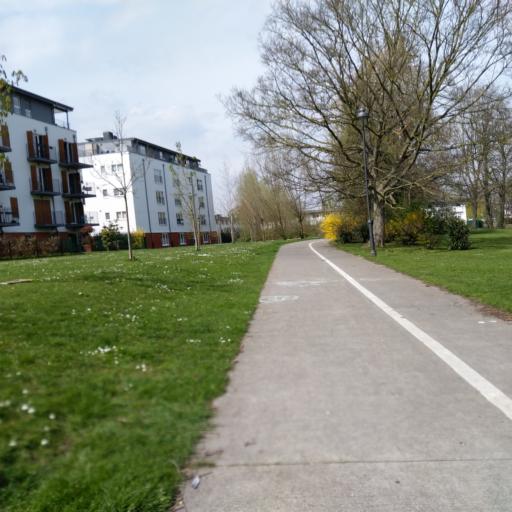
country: BE
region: Wallonia
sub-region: Province du Hainaut
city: Mons
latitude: 50.4459
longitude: 3.9619
